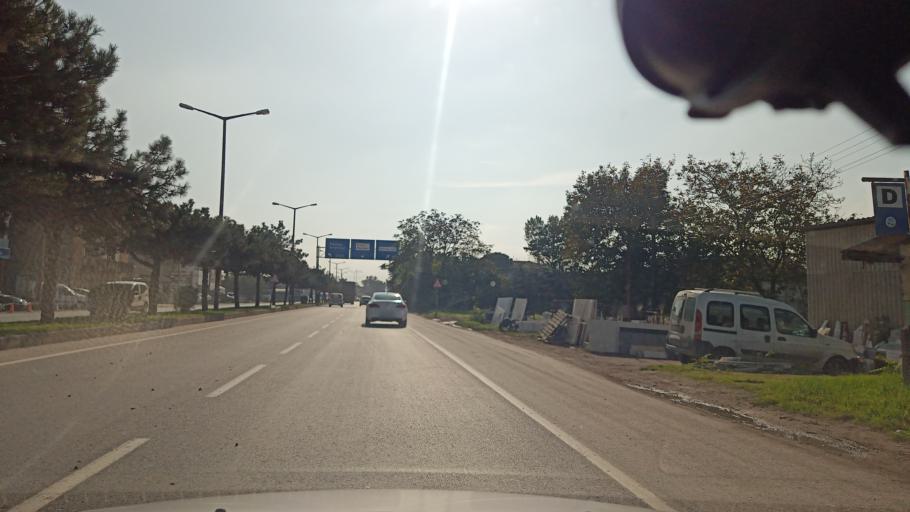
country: TR
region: Sakarya
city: Adapazari
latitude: 40.8034
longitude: 30.4060
